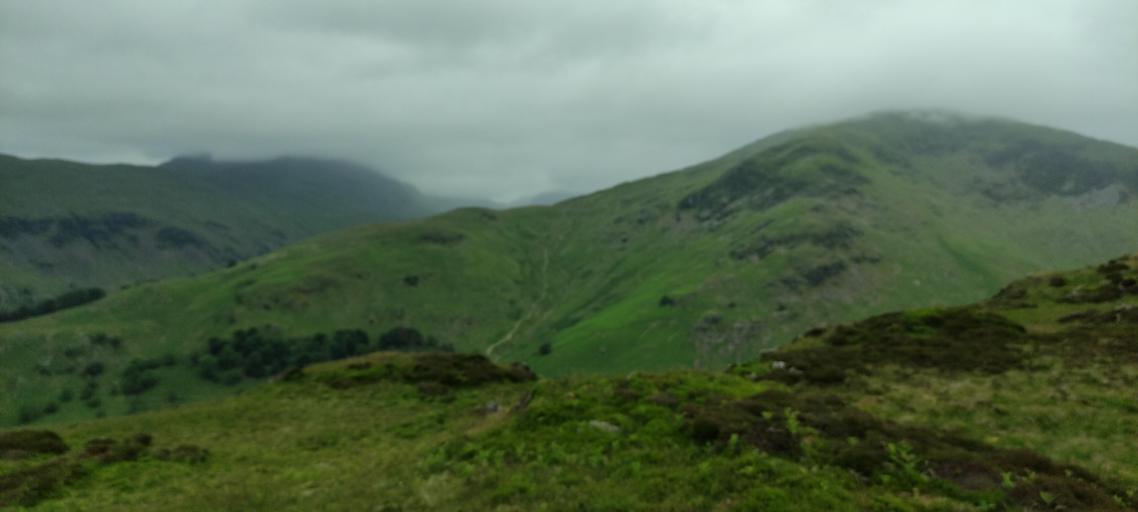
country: GB
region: England
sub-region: Cumbria
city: Ambleside
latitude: 54.5493
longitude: -2.9580
